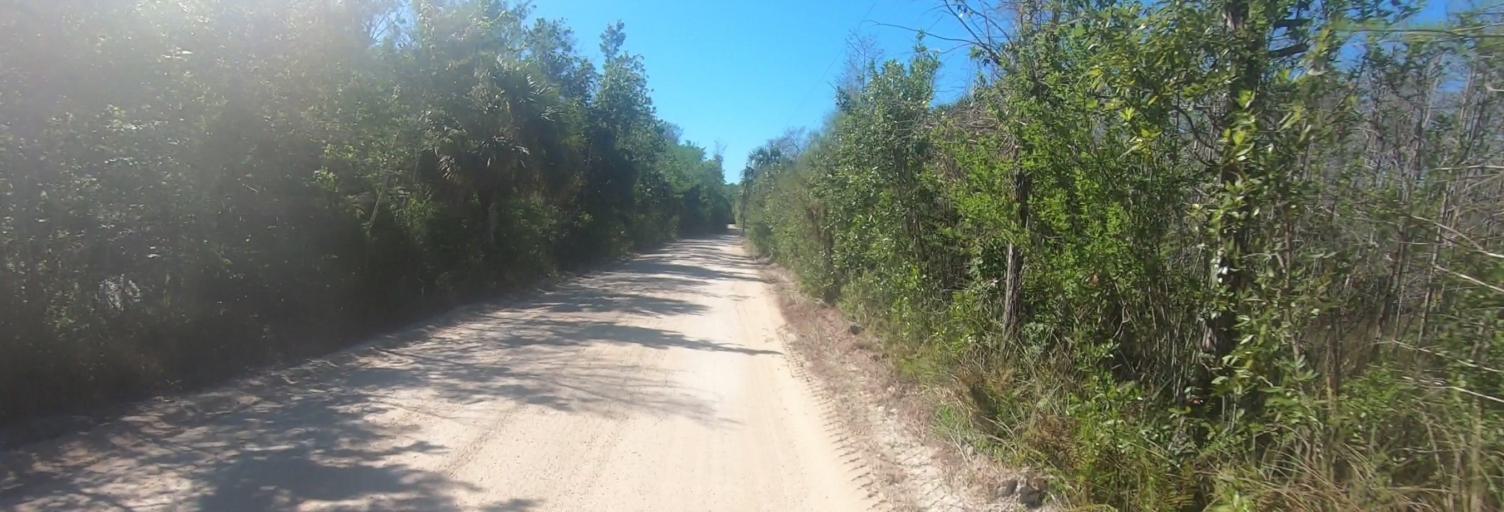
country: US
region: Florida
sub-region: Collier County
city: Marco
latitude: 25.8802
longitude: -81.2299
